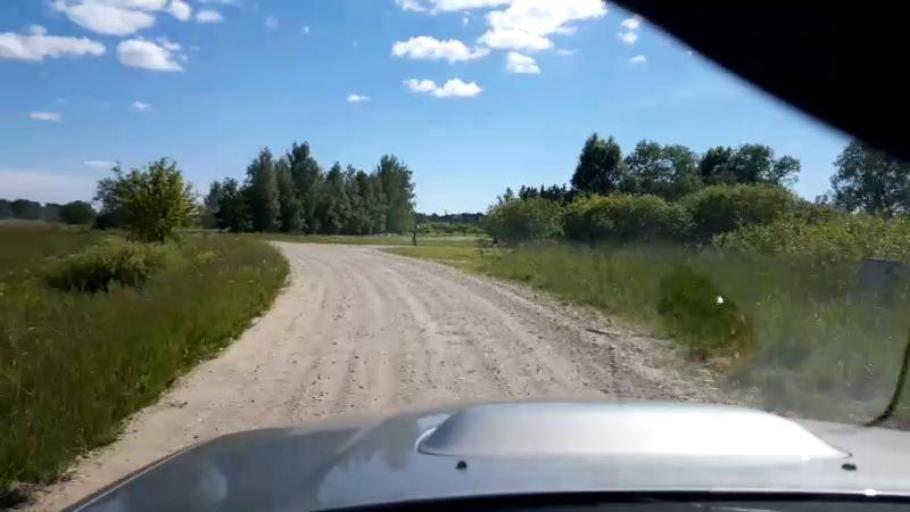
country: EE
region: Paernumaa
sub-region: Sauga vald
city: Sauga
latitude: 58.5104
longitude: 24.5139
